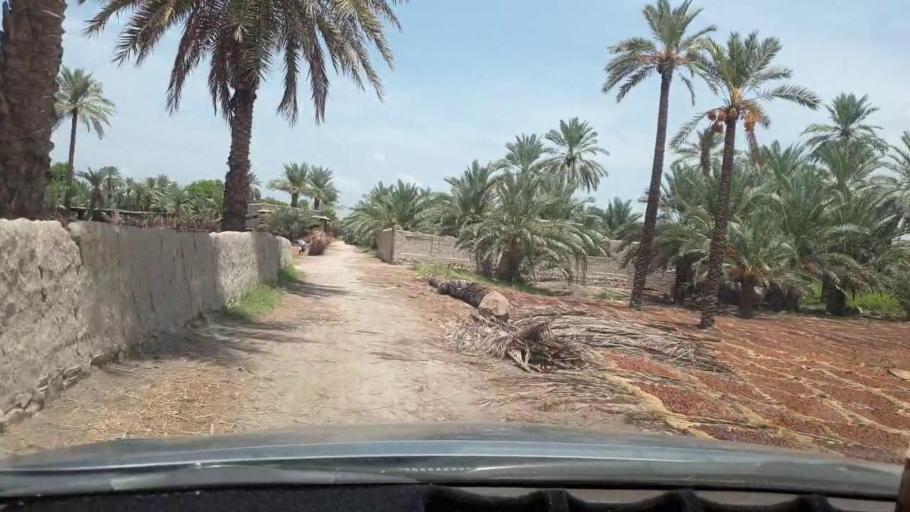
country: PK
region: Sindh
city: Khairpur
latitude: 27.4465
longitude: 68.7778
